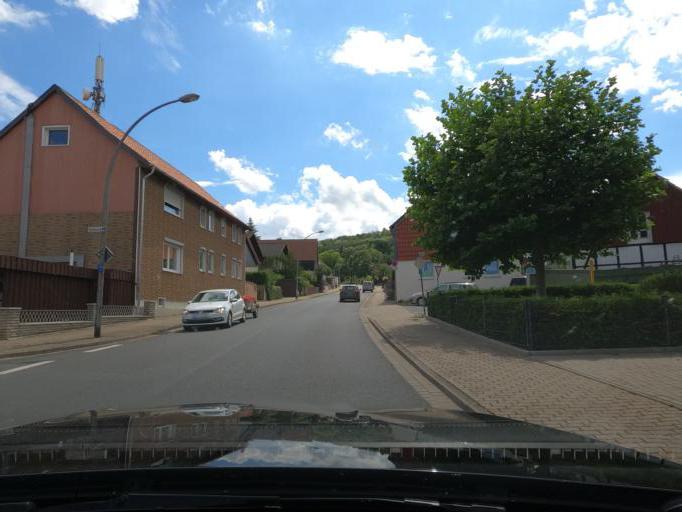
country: DE
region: Lower Saxony
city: Elbe
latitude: 52.1274
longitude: 10.2903
